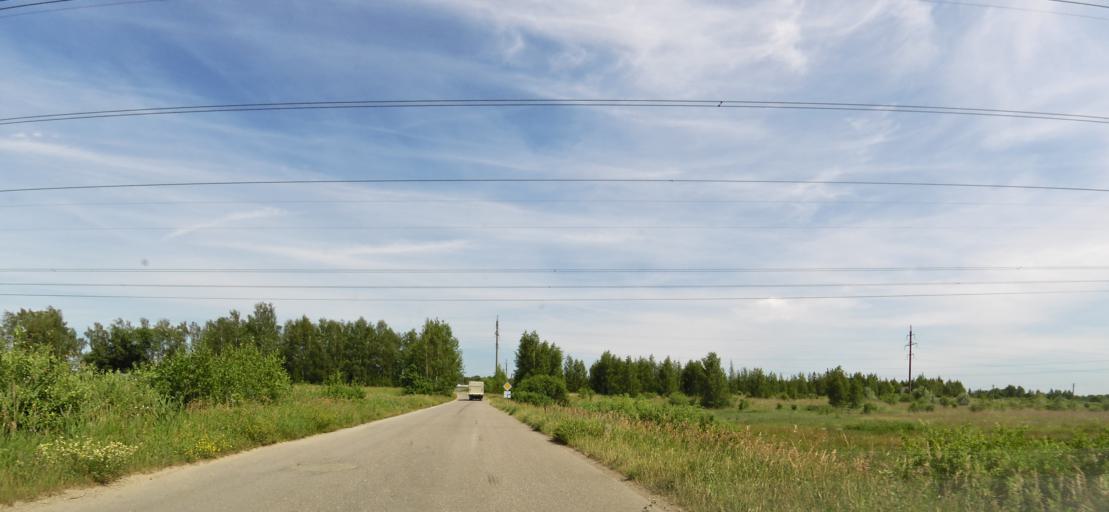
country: LT
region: Panevezys
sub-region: Panevezys City
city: Panevezys
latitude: 55.7178
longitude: 24.2808
